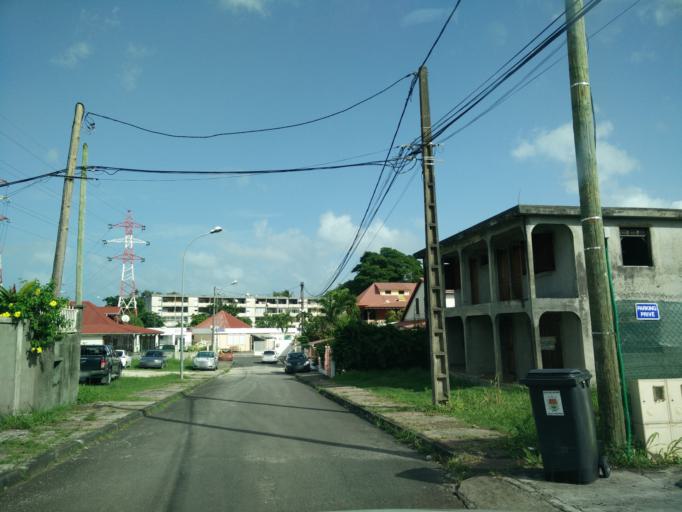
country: GP
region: Guadeloupe
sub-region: Guadeloupe
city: Les Abymes
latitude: 16.2531
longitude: -61.5154
